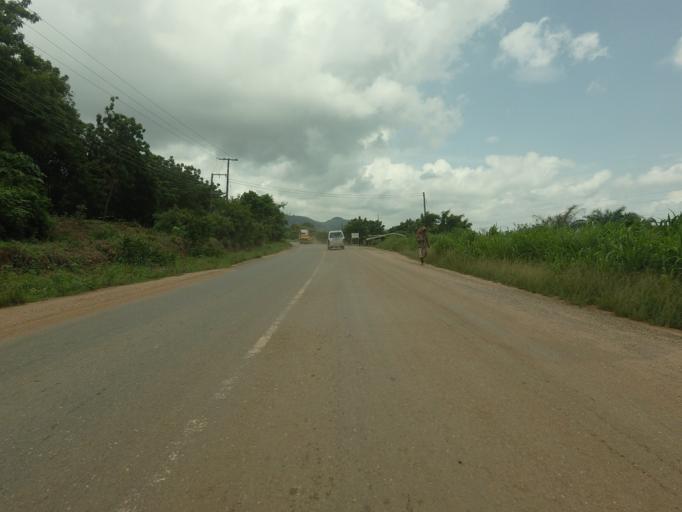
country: GH
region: Volta
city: Ho
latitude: 6.7061
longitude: 0.3341
